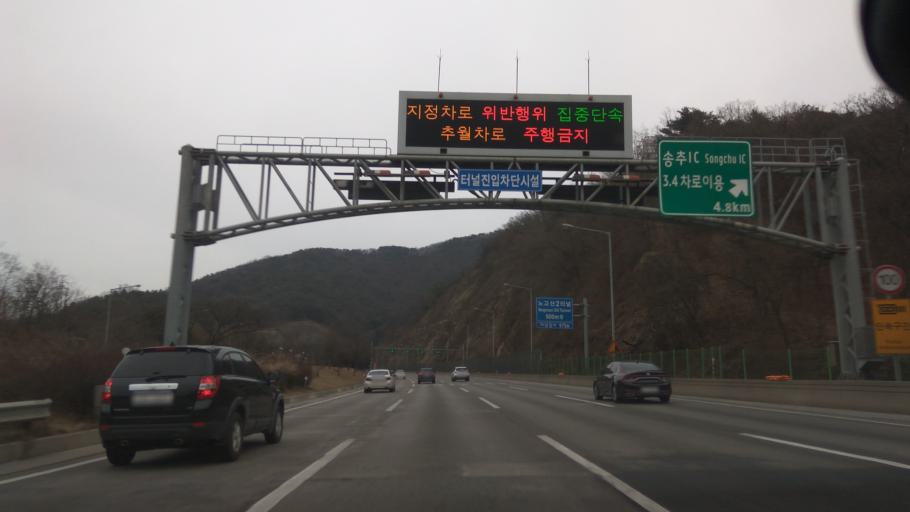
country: KR
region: Gyeonggi-do
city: Jangheung
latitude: 37.6837
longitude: 126.9304
